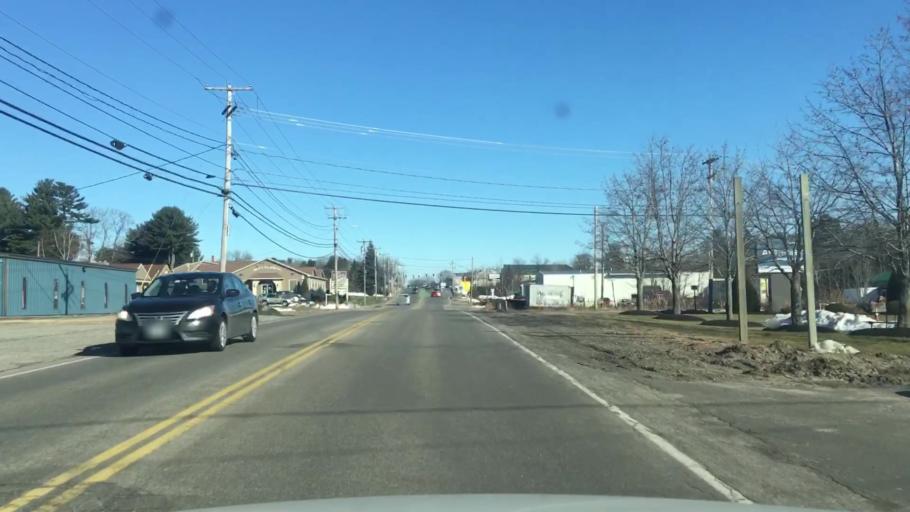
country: US
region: Maine
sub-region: York County
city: Biddeford
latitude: 43.4663
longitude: -70.4879
